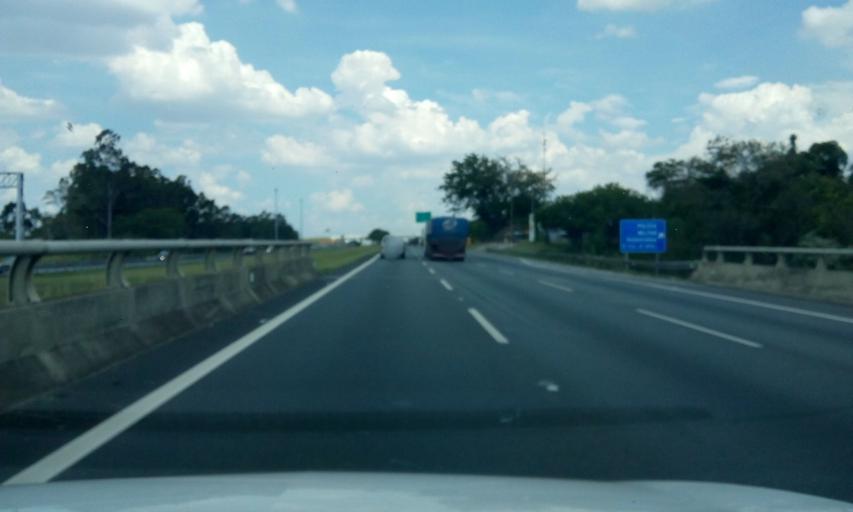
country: BR
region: Sao Paulo
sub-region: Valinhos
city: Valinhos
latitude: -23.0098
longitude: -47.0917
